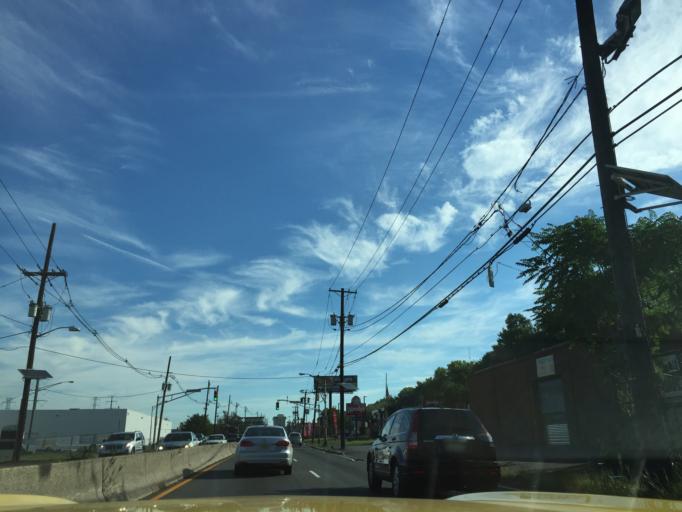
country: US
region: New Jersey
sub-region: Hudson County
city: Secaucus
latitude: 40.7655
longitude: -74.0474
